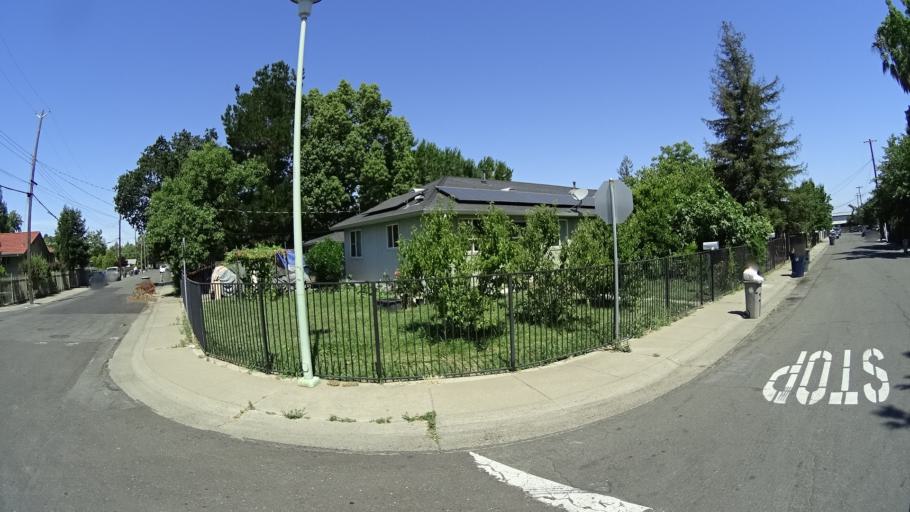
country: US
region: California
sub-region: Sacramento County
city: Florin
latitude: 38.5359
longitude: -121.4141
